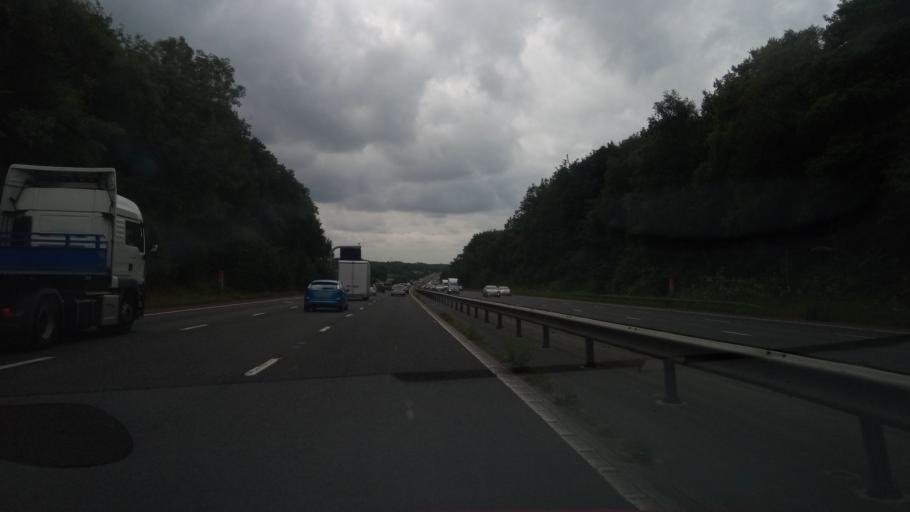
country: GB
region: England
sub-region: Lancashire
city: Galgate
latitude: 54.0092
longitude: -2.7810
